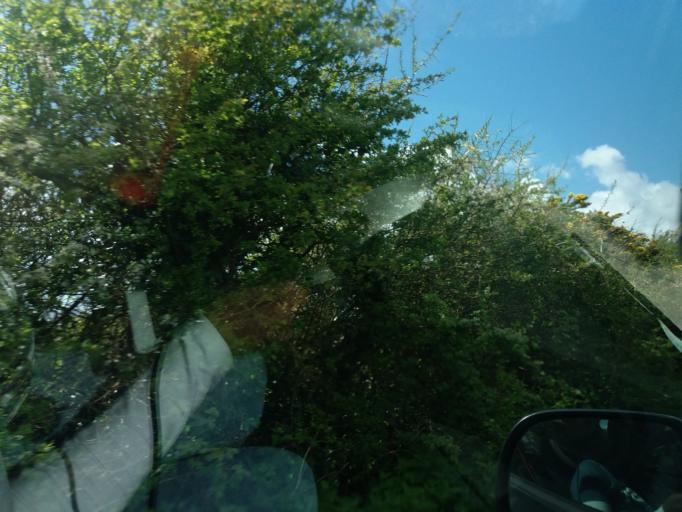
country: IE
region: Munster
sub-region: Waterford
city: Dunmore East
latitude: 52.2135
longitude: -6.9058
